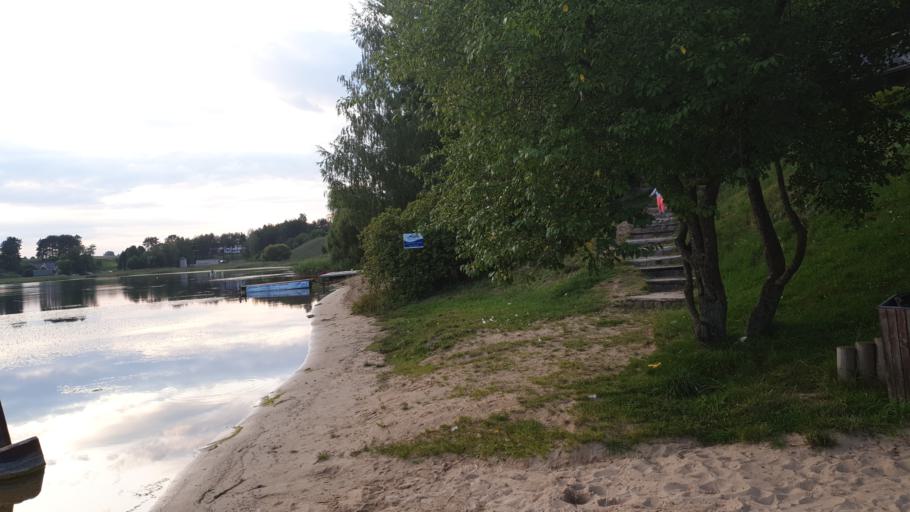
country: LT
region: Vilnius County
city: Pilaite
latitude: 54.7058
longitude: 25.1593
